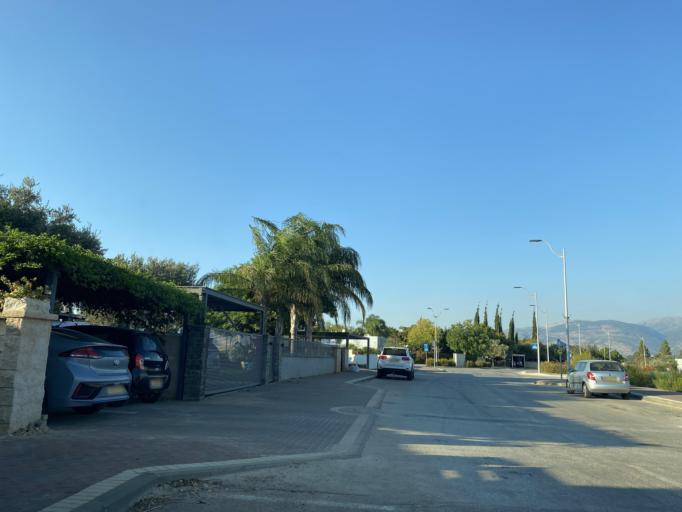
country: IL
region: Northern District
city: Qiryat Shemona
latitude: 33.1746
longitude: 35.6064
